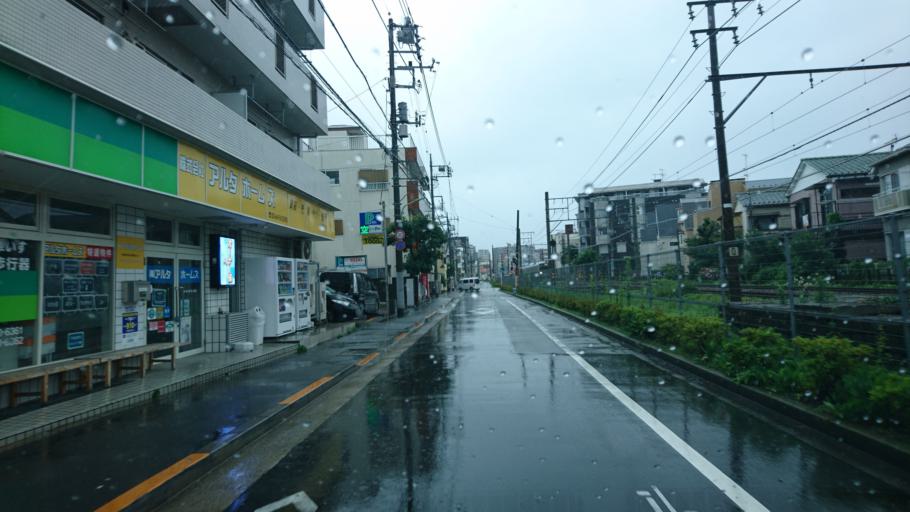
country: JP
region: Kanagawa
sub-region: Kawasaki-shi
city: Kawasaki
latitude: 35.5690
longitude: 139.7065
